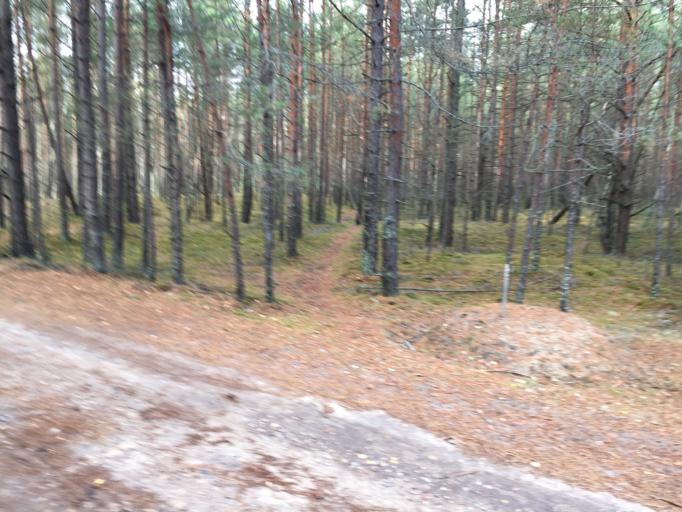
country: LV
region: Carnikava
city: Carnikava
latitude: 57.1499
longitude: 24.2593
